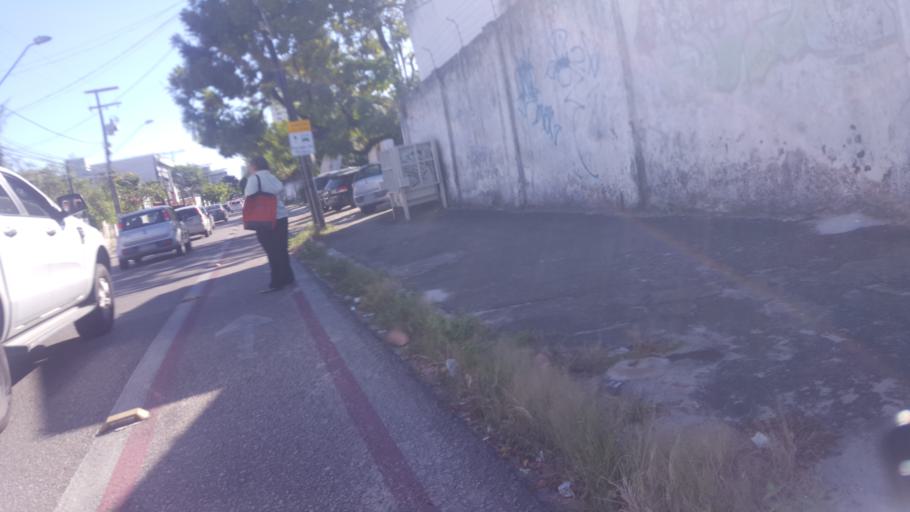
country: BR
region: Ceara
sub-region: Fortaleza
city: Fortaleza
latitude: -3.7446
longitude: -38.5340
